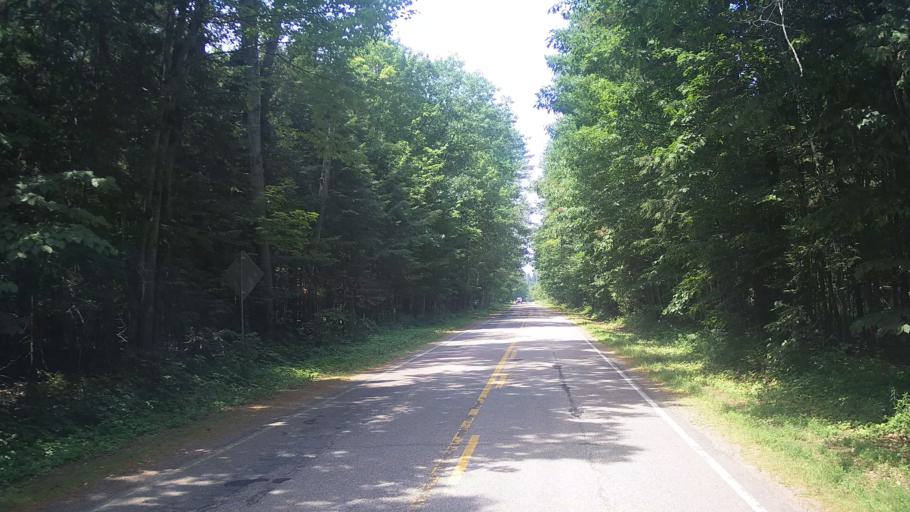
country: CA
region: Quebec
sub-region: Outaouais
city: Shawville
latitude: 45.5227
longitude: -76.4364
